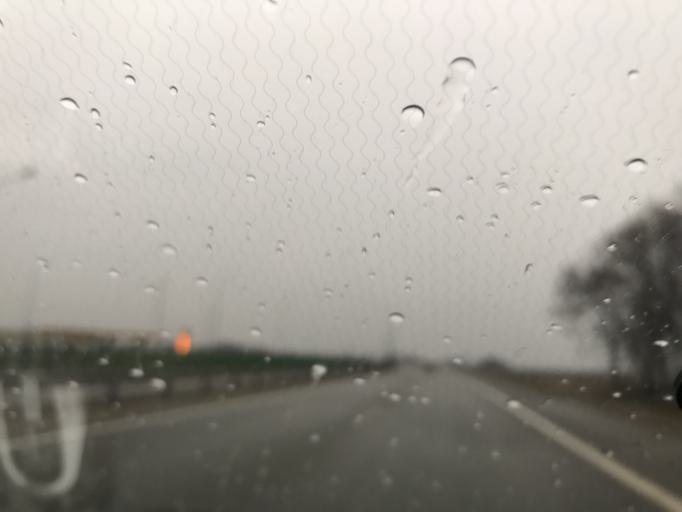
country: RU
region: Krasnodarskiy
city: Krylovskaya
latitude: 46.2781
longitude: 39.8317
